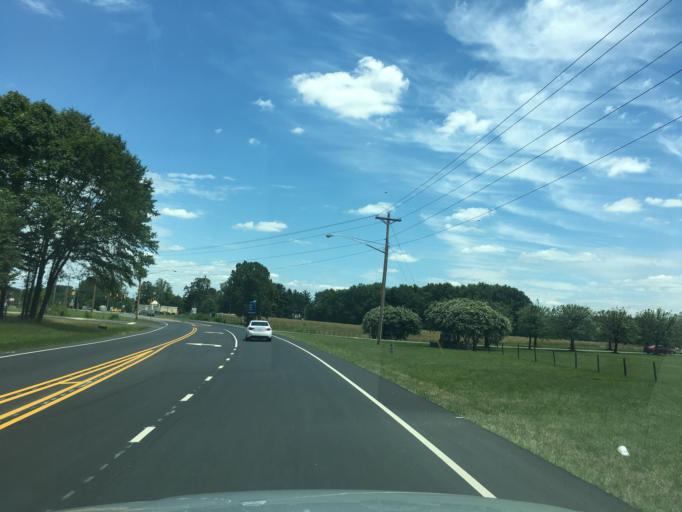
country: US
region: North Carolina
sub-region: Burke County
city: Morganton
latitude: 35.7332
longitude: -81.7283
